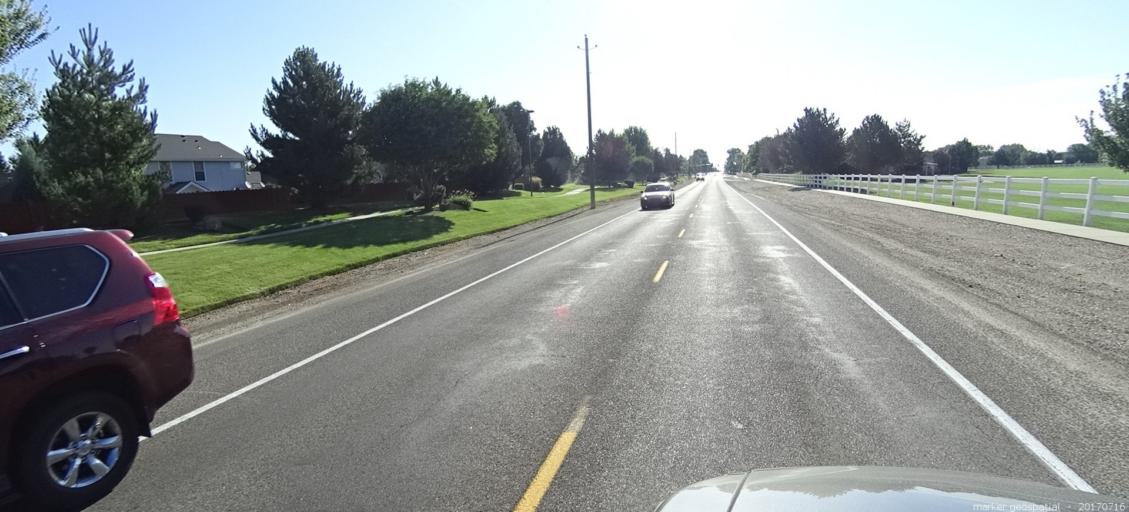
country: US
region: Idaho
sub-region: Ada County
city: Meridian
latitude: 43.5466
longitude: -116.3382
